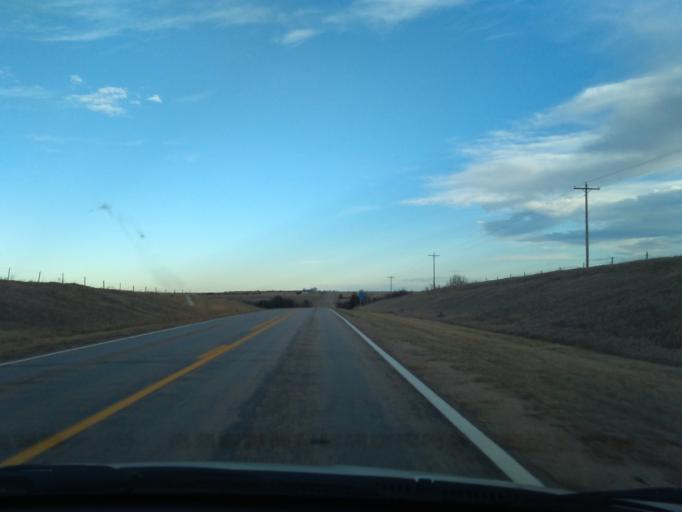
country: US
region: Nebraska
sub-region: Phelps County
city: Holdrege
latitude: 40.3072
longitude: -99.3543
